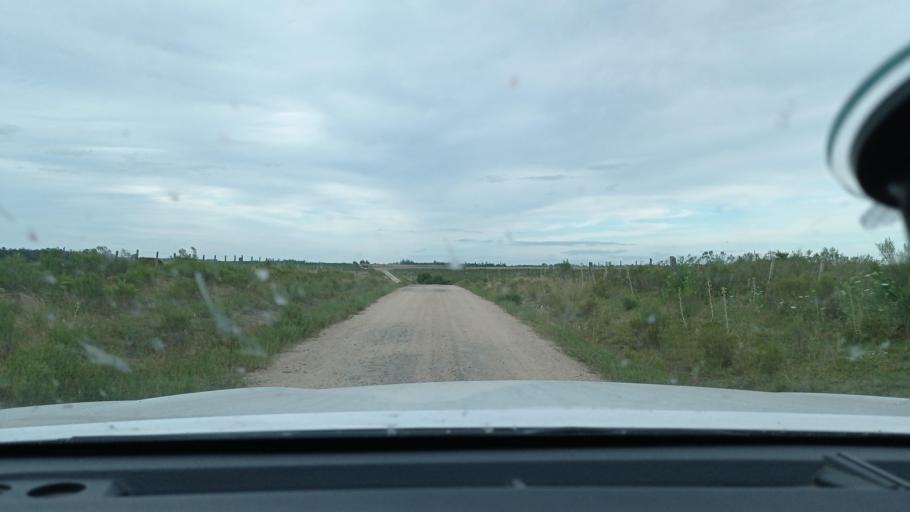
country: UY
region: Florida
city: Casupa
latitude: -34.1444
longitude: -55.7897
